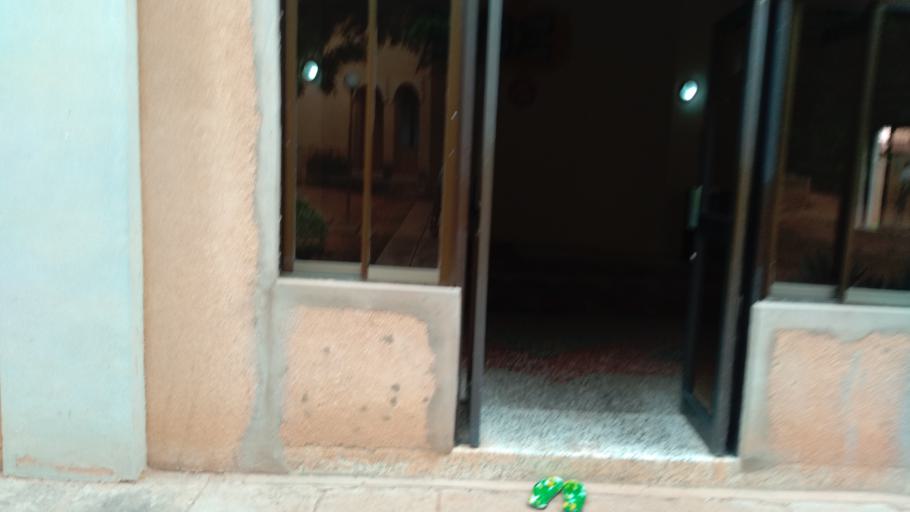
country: NG
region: Katsina
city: Katsina
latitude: 12.9620
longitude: 7.6391
